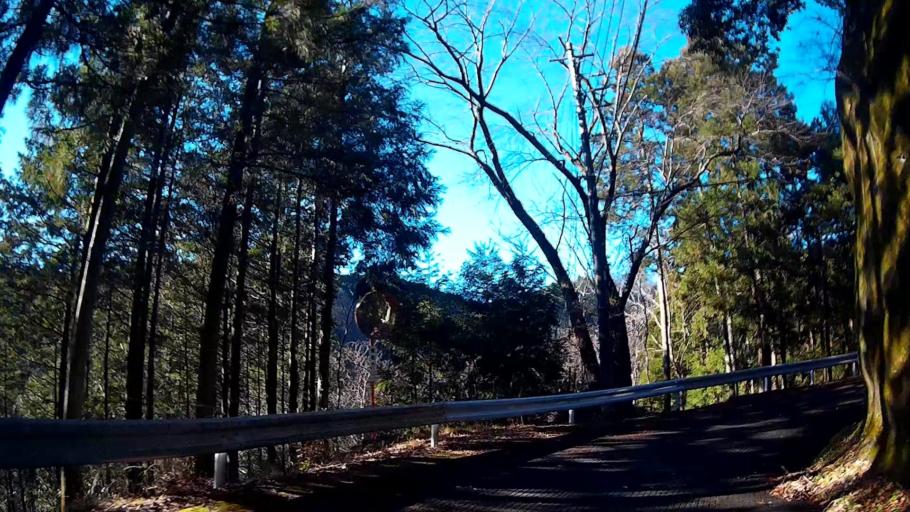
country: JP
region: Saitama
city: Chichibu
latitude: 35.9444
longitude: 139.1749
